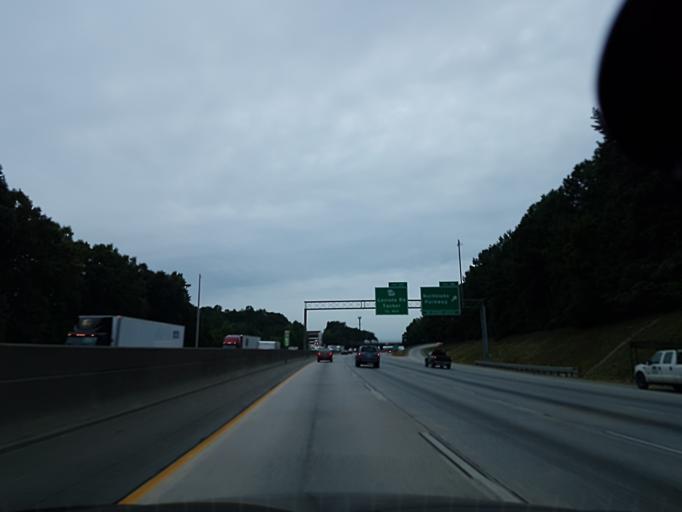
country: US
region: Georgia
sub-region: DeKalb County
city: Tucker
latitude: 33.8553
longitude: -84.2466
